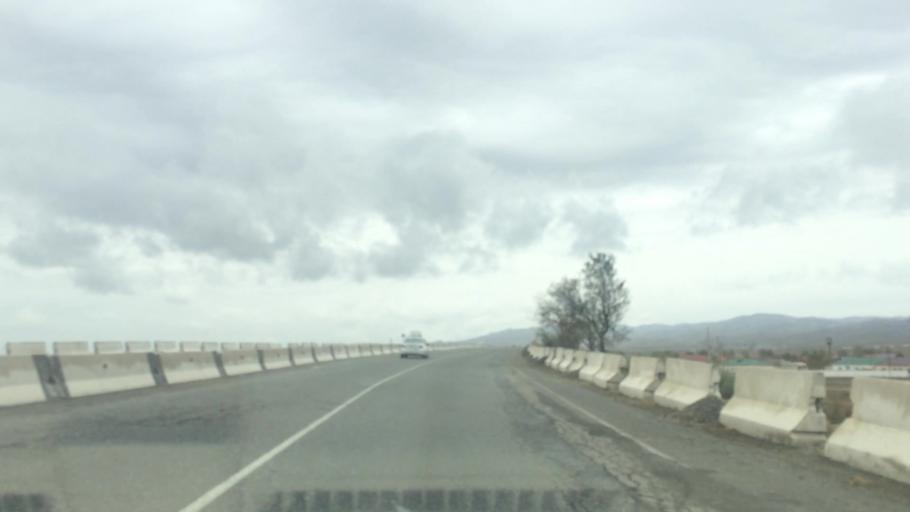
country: UZ
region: Samarqand
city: Bulung'ur
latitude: 39.8367
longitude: 67.4393
